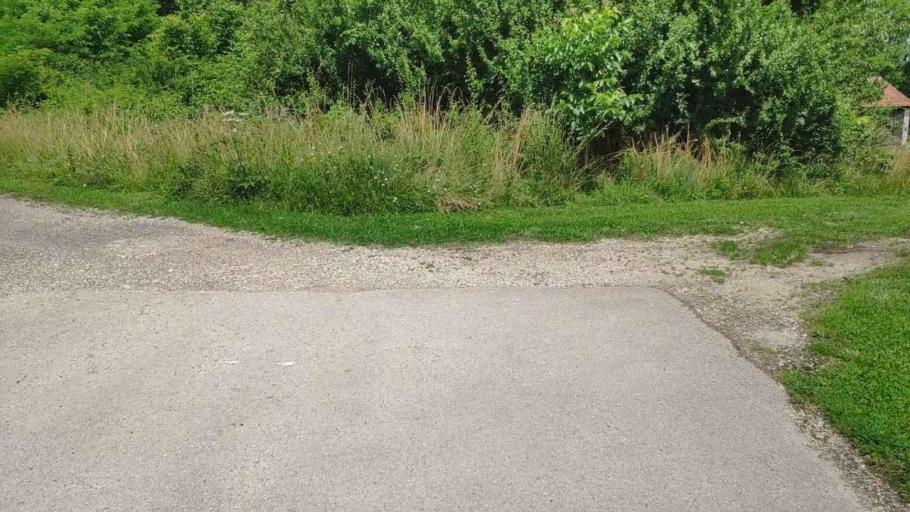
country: FR
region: Franche-Comte
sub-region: Departement du Jura
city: Bletterans
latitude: 46.8479
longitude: 5.4838
